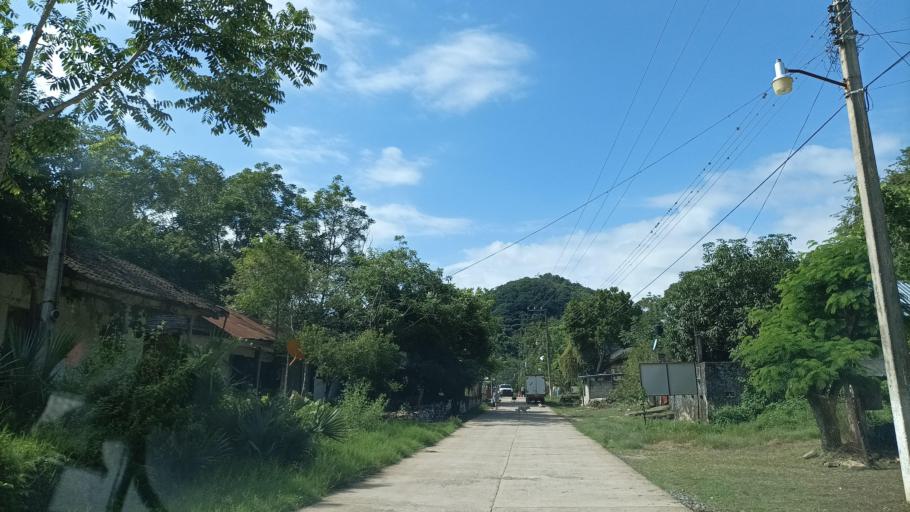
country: MX
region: Hidalgo
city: Huautla
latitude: 21.1334
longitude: -98.2503
